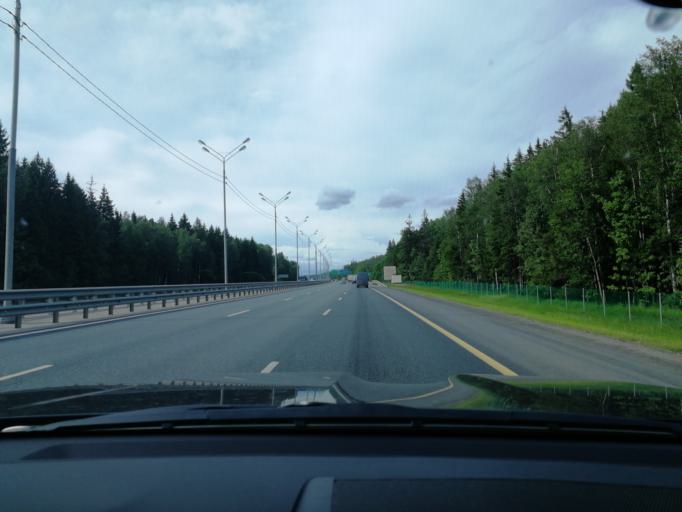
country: RU
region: Moskovskaya
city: Novyy Byt
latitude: 55.0197
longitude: 37.5573
